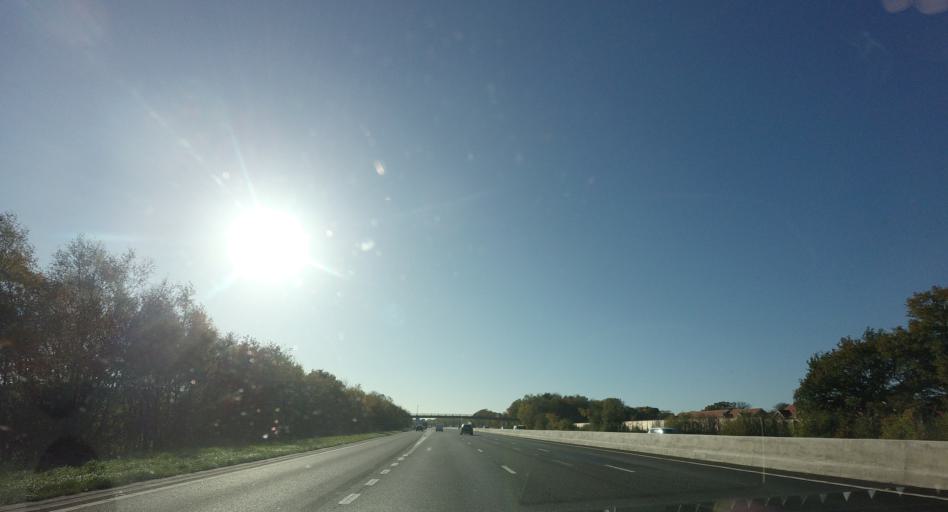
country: GB
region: England
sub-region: West Sussex
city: Copthorne
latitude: 51.1394
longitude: -0.1391
